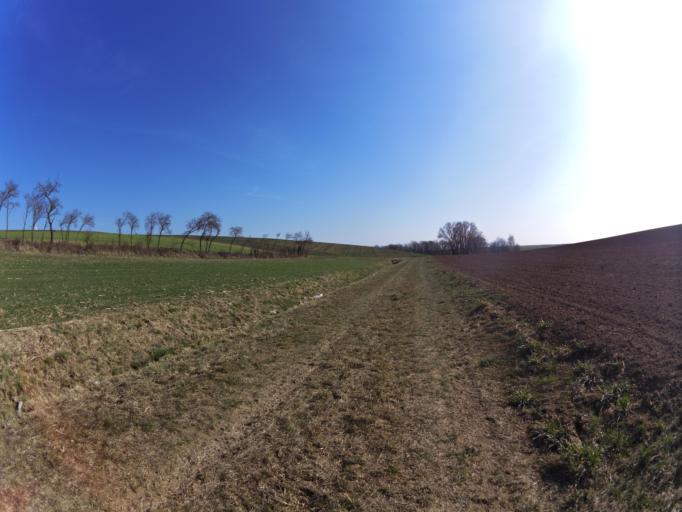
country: DE
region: Bavaria
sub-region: Regierungsbezirk Unterfranken
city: Dettelbach
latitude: 49.8284
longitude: 10.1376
